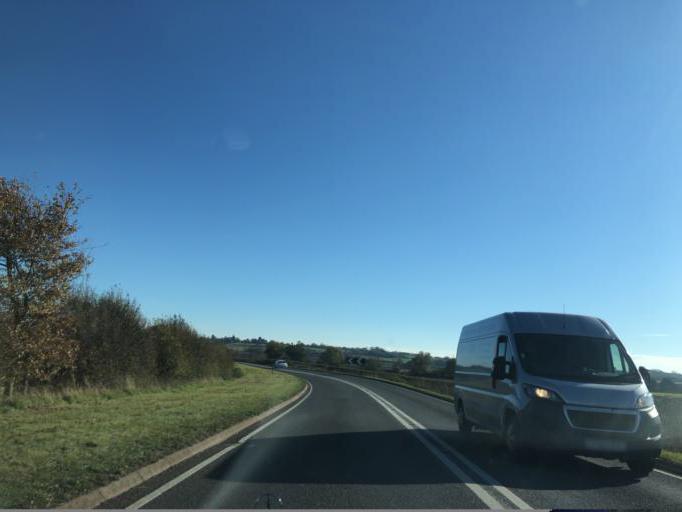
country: GB
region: England
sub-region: Warwickshire
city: Harbury
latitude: 52.2665
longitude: -1.4686
